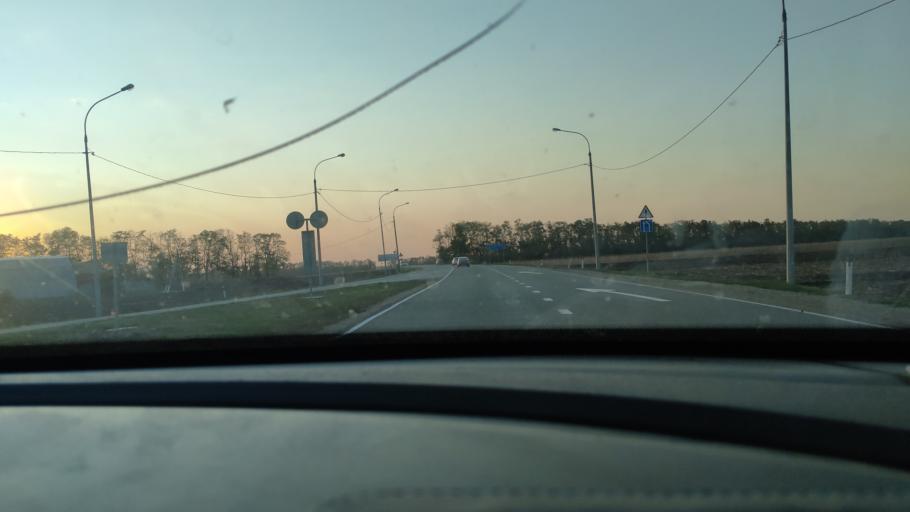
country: RU
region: Krasnodarskiy
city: Starominskaya
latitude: 46.4929
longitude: 39.0584
